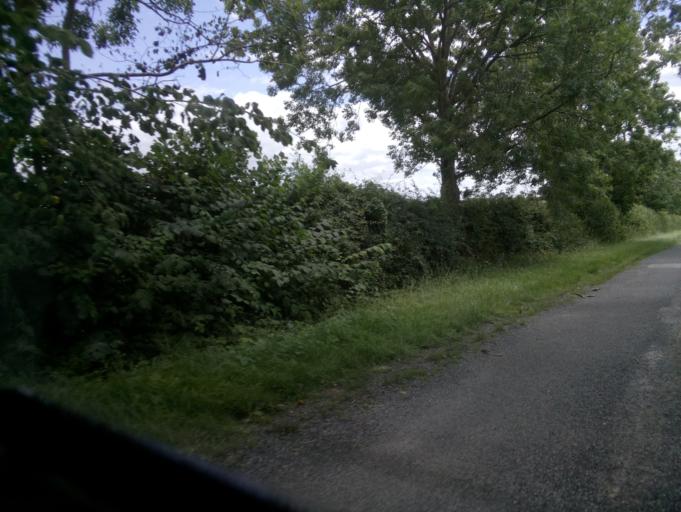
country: GB
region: England
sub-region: Nottinghamshire
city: Cotgrave
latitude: 52.8609
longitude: -1.0565
